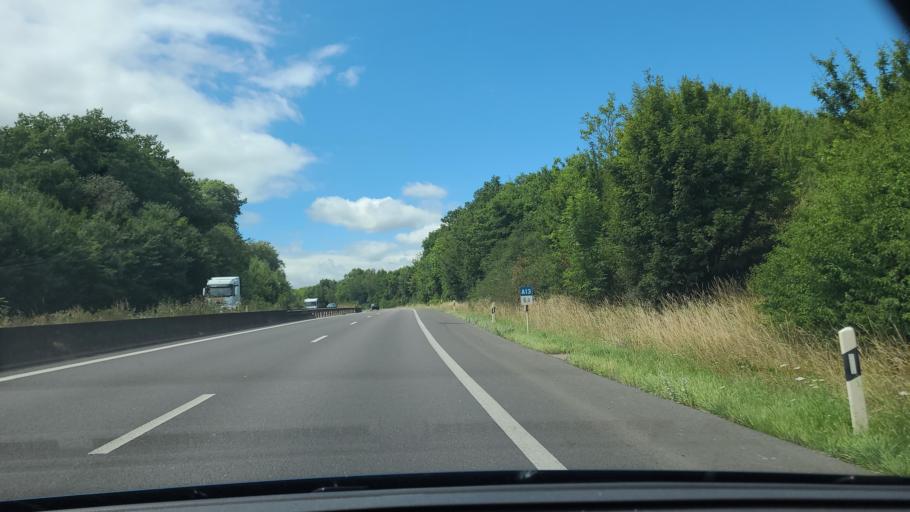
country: LU
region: Luxembourg
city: Soleuvre
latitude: 49.5306
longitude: 5.9553
